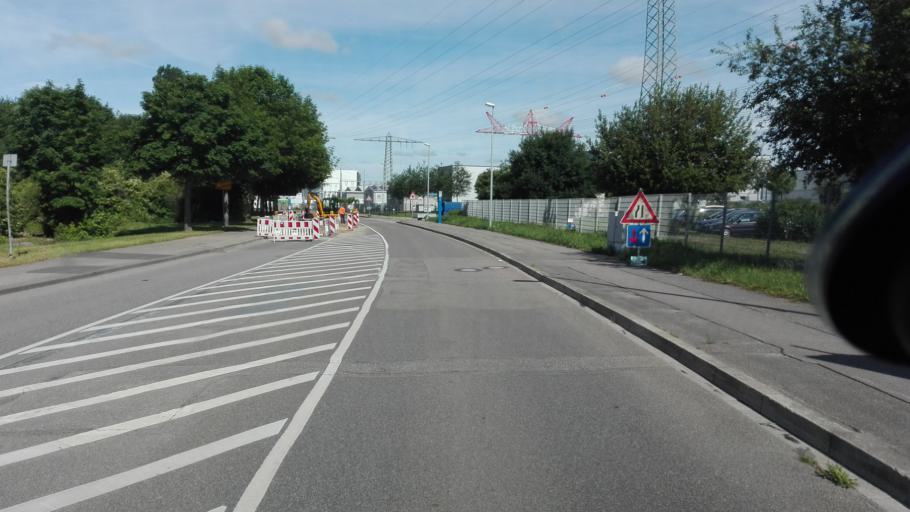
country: DE
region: Baden-Wuerttemberg
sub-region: Karlsruhe Region
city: Forst
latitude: 49.1312
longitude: 8.5657
